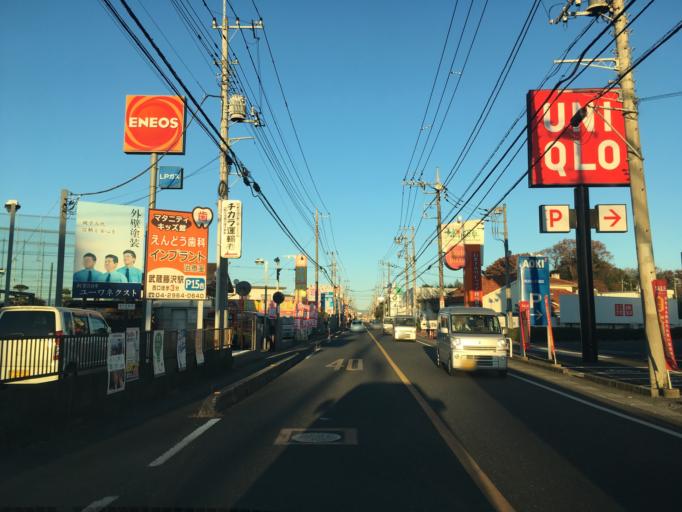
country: JP
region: Saitama
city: Tokorozawa
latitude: 35.8094
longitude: 139.4339
